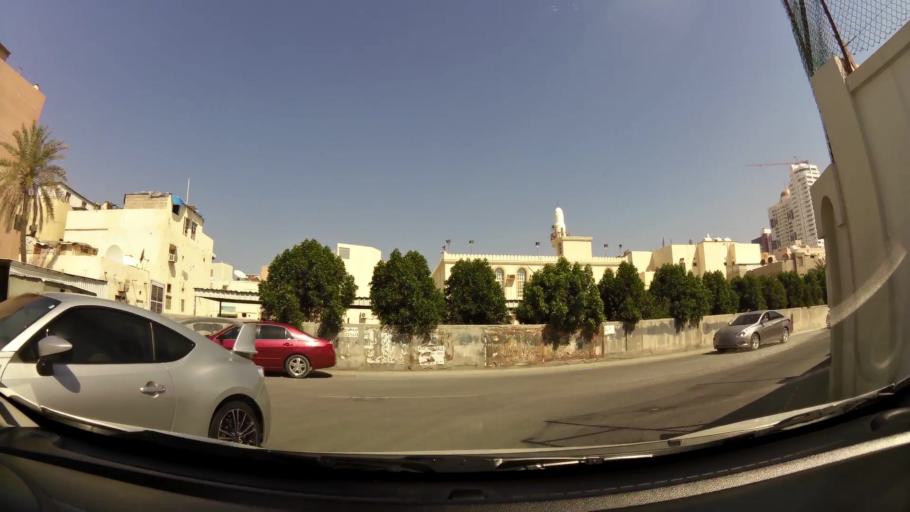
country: BH
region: Manama
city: Manama
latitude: 26.2103
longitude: 50.6033
